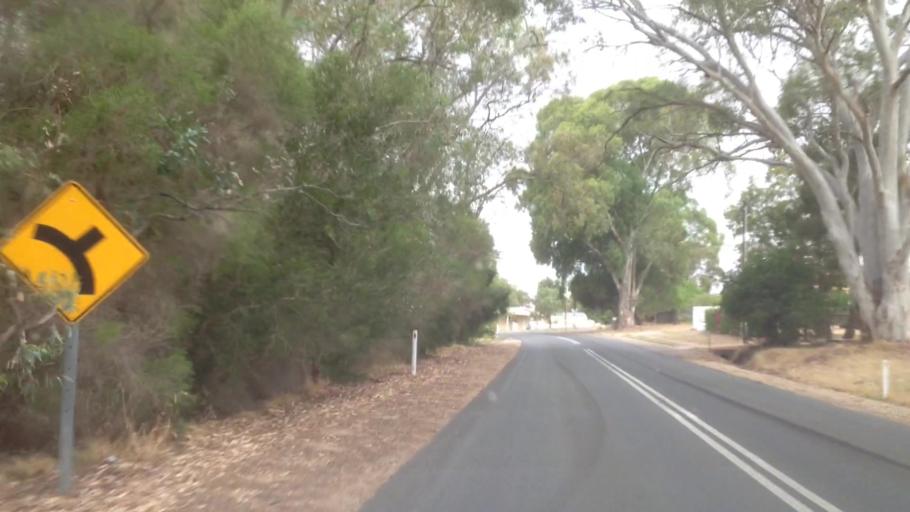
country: AU
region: South Australia
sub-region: Barossa
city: Williamstown
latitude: -34.6676
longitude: 138.8762
